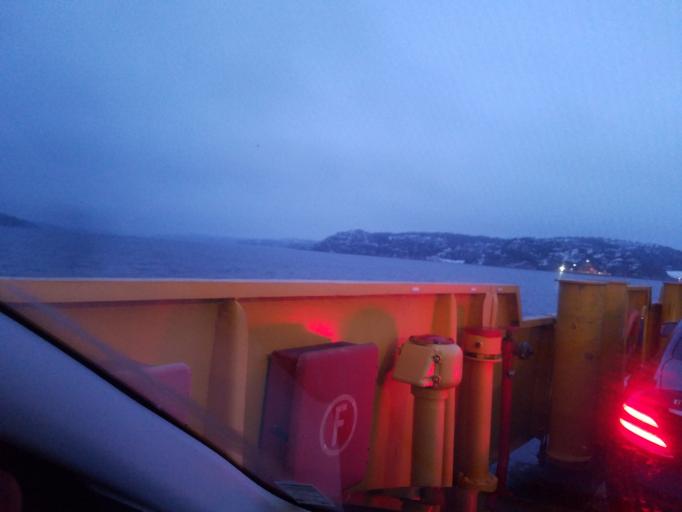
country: SE
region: Vaestra Goetaland
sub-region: Lysekils Kommun
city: Lysekil
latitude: 58.3010
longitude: 11.5177
